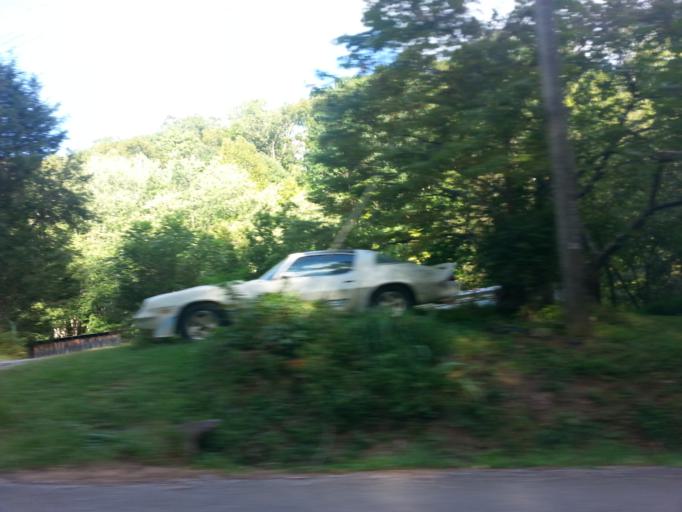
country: US
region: Tennessee
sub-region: Knox County
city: Mascot
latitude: 36.1116
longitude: -83.7507
